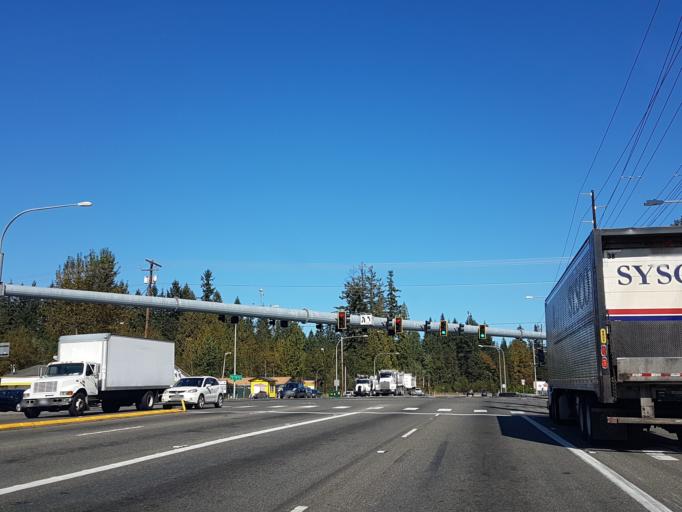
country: US
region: Washington
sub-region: Snohomish County
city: Maltby
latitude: 47.8043
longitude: -122.1433
